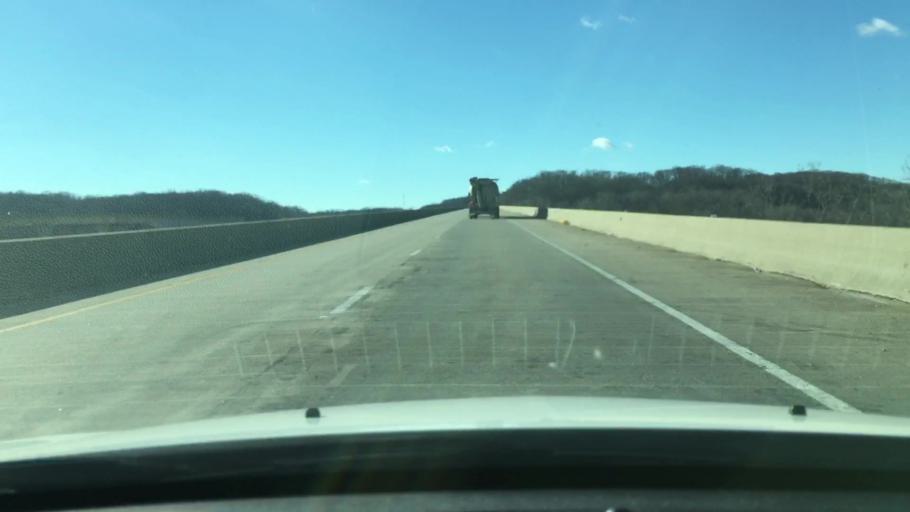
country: US
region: Illinois
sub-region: Pike County
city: Griggsville
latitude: 39.6904
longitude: -90.6350
